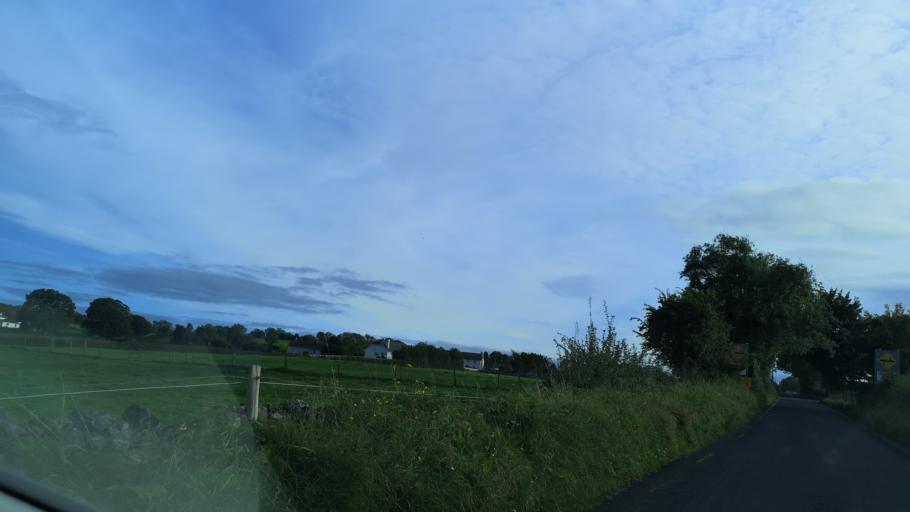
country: IE
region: Connaught
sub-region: County Galway
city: Ballinasloe
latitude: 53.3285
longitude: -8.2773
